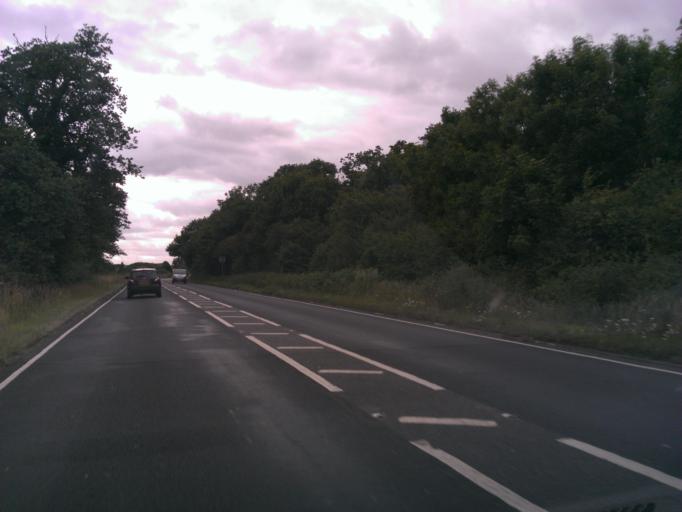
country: GB
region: England
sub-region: Essex
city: Great Bentley
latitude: 51.8639
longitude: 1.0855
